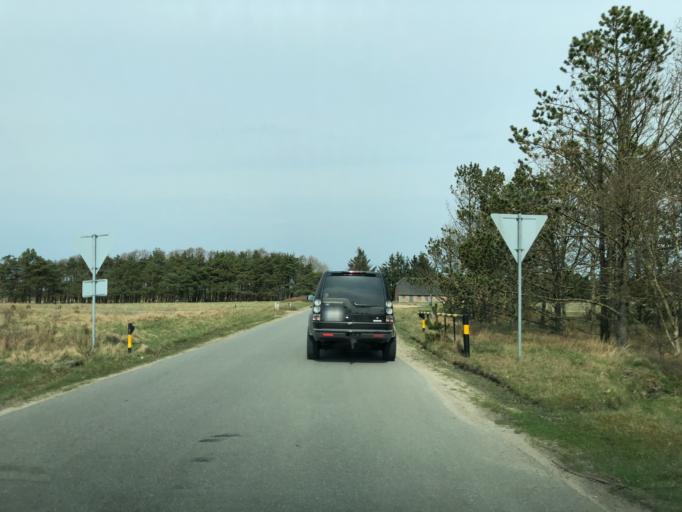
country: DK
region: South Denmark
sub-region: Varde Kommune
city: Oksbol
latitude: 55.6182
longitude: 8.1684
